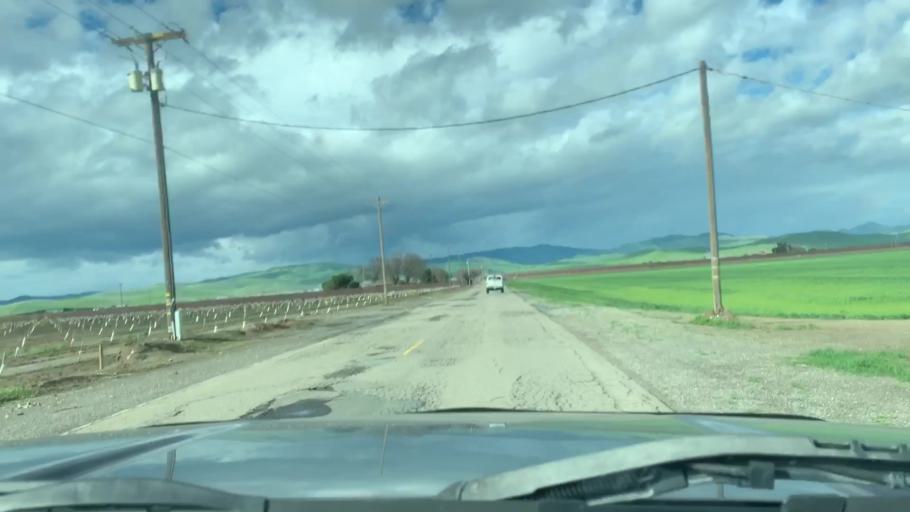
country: US
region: California
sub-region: Merced County
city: Gustine
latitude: 37.1224
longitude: -121.0068
